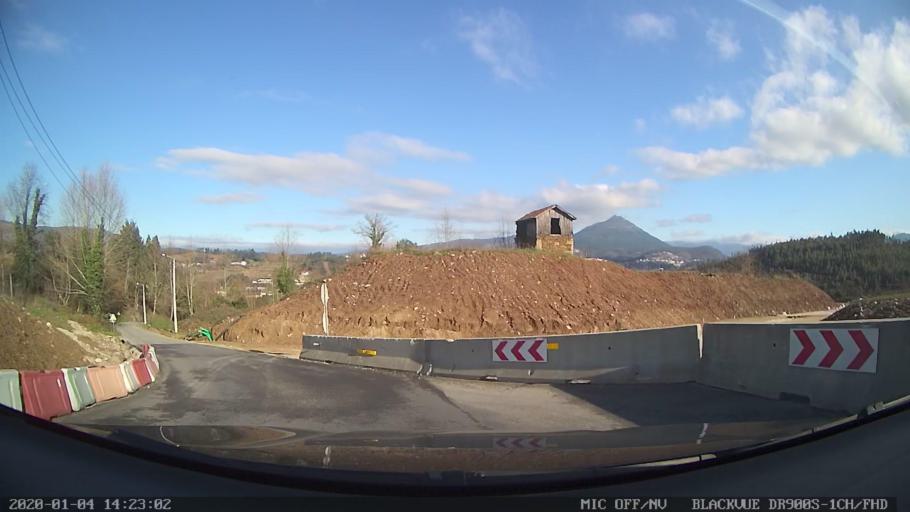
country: PT
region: Braga
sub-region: Celorico de Basto
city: Celorico de Basto
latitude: 41.4089
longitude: -7.9838
